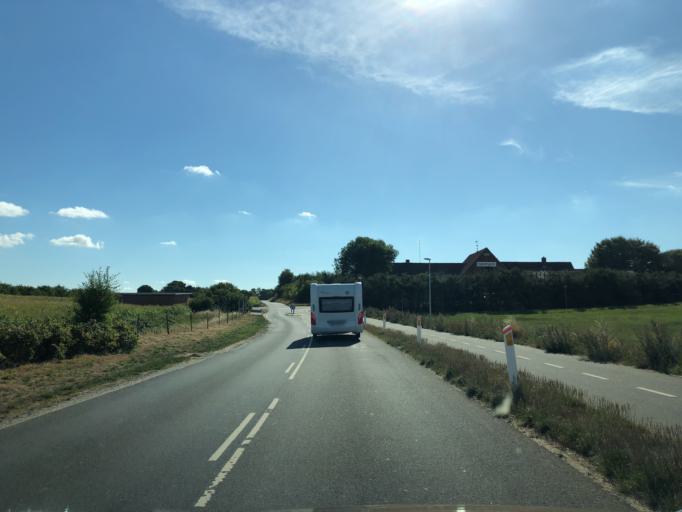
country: DK
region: Central Jutland
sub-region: Silkeborg Kommune
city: Silkeborg
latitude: 56.1505
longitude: 9.4614
